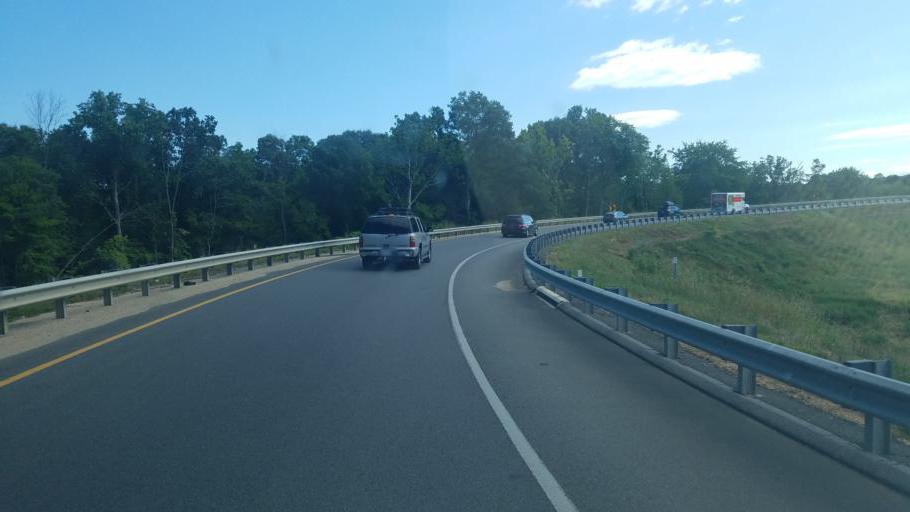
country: US
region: Virginia
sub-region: Fauquier County
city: Bealeton
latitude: 38.6140
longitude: -77.8025
